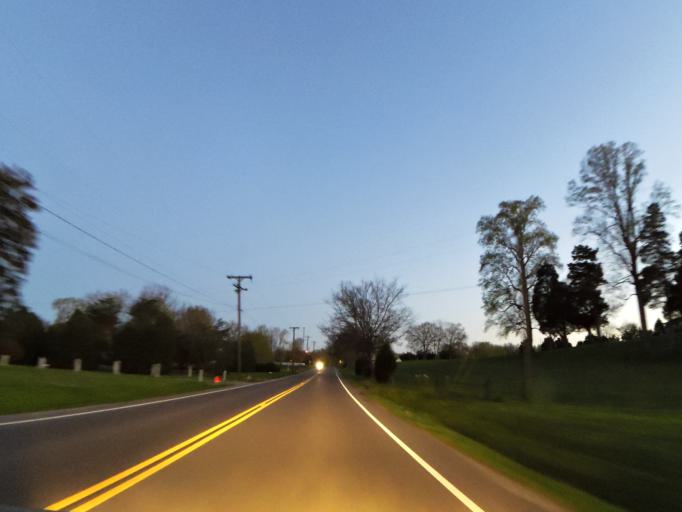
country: US
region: Tennessee
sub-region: Robertson County
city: Coopertown
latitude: 36.3796
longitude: -86.8939
